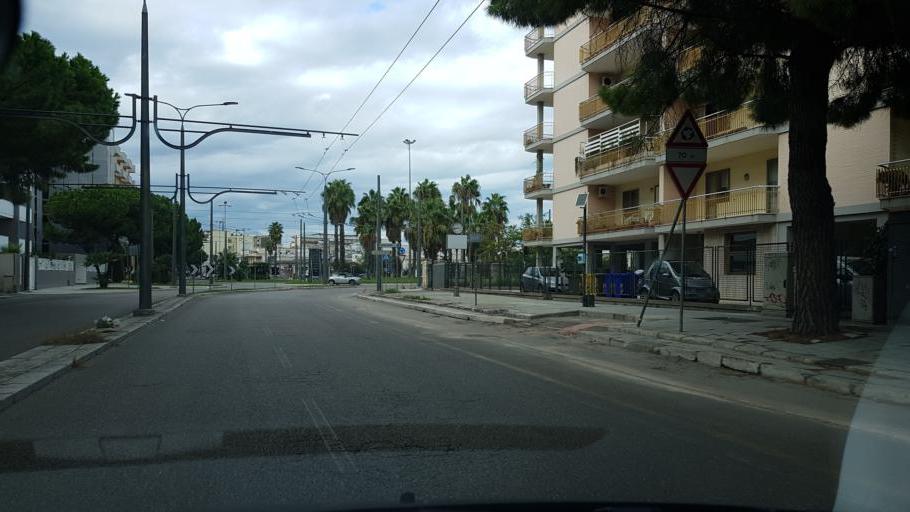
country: IT
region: Apulia
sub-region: Provincia di Lecce
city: Lecce
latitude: 40.3580
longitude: 18.1834
